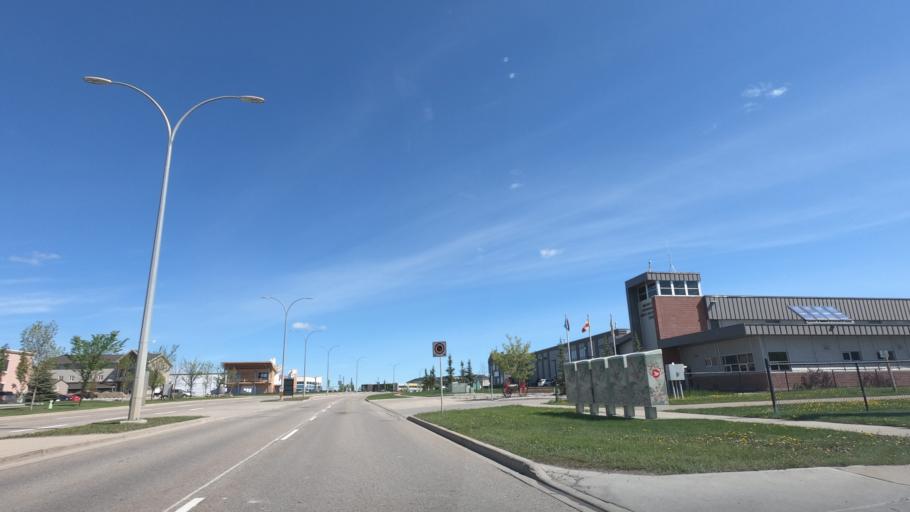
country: CA
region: Alberta
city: Airdrie
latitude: 51.2626
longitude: -113.9952
